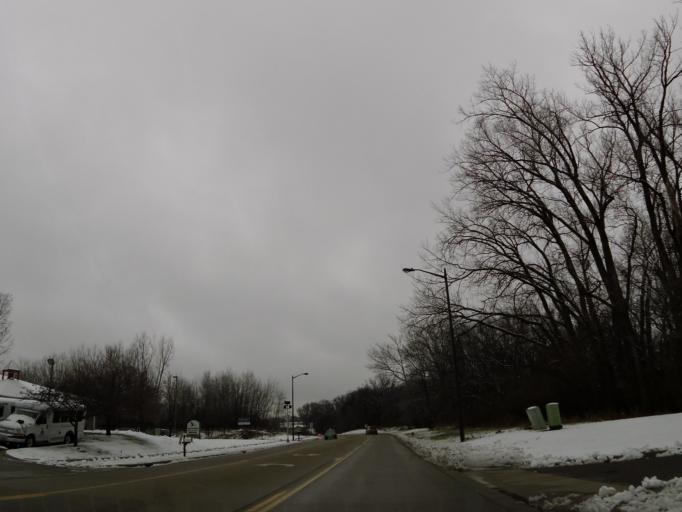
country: US
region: Minnesota
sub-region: Dakota County
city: Lakeville
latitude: 44.6963
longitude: -93.2841
